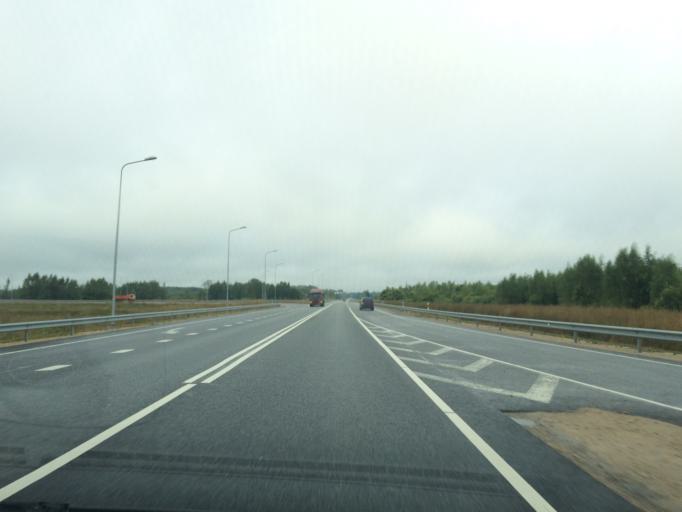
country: LV
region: Lielvarde
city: Lielvarde
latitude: 56.8071
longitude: 24.8800
